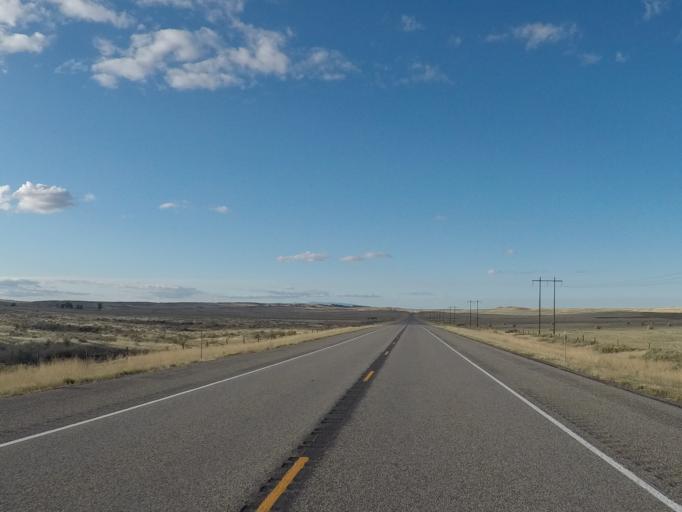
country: US
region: Montana
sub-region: Golden Valley County
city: Ryegate
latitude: 46.1970
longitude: -108.9173
